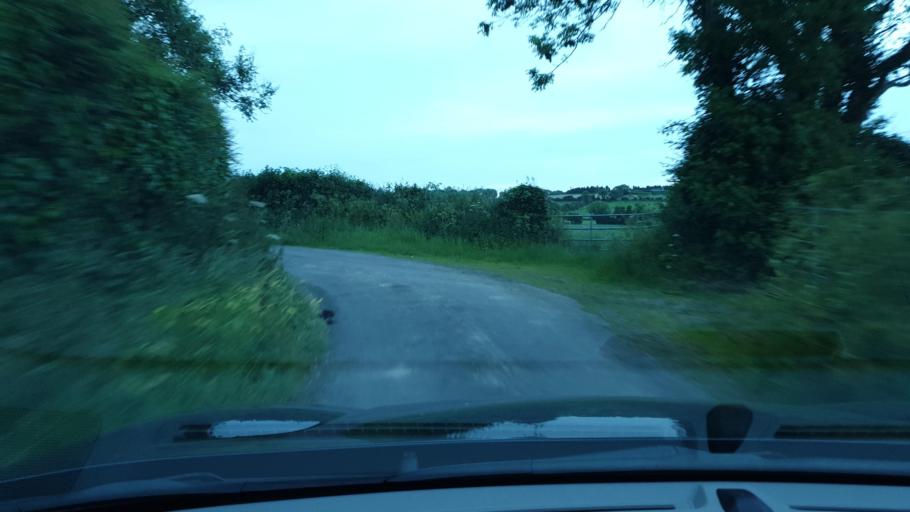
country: IE
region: Leinster
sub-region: An Mhi
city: Duleek
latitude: 53.5973
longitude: -6.3611
